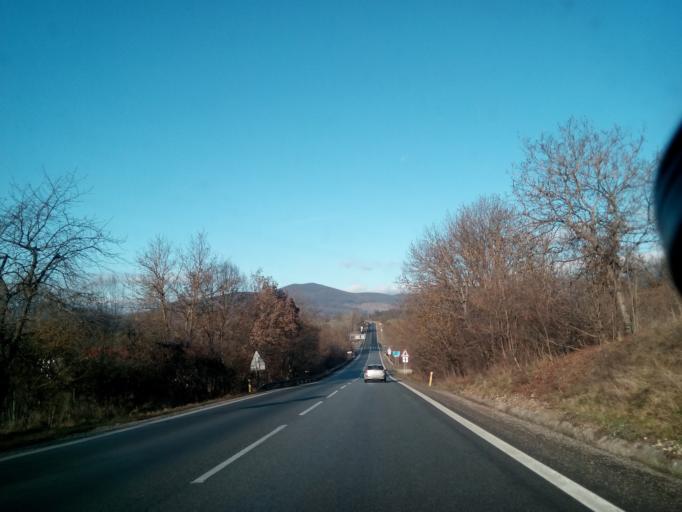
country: SK
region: Kosicky
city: Roznava
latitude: 48.6320
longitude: 20.6183
